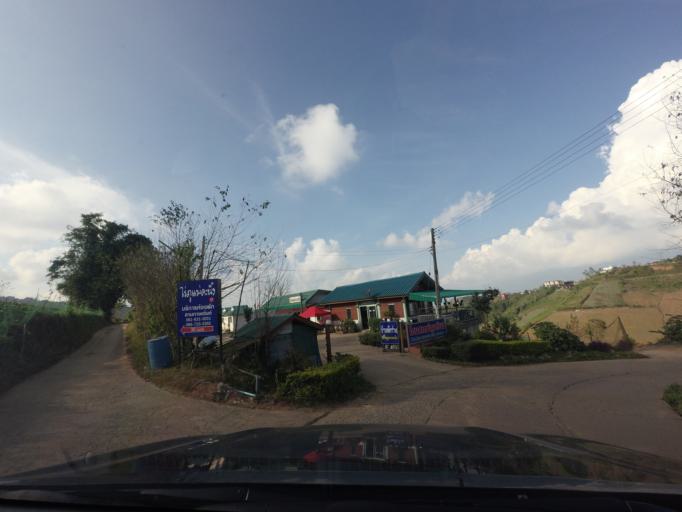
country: TH
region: Phetchabun
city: Lom Kao
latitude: 16.9029
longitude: 101.1067
